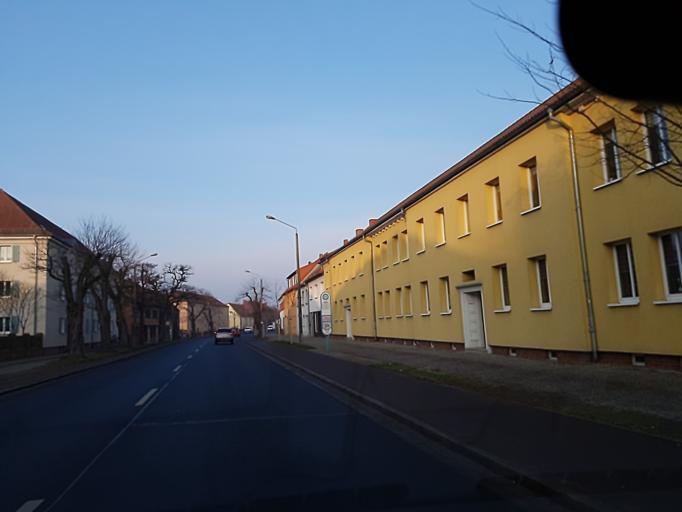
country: DE
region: Saxony-Anhalt
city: Wittenburg
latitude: 51.8677
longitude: 12.5911
